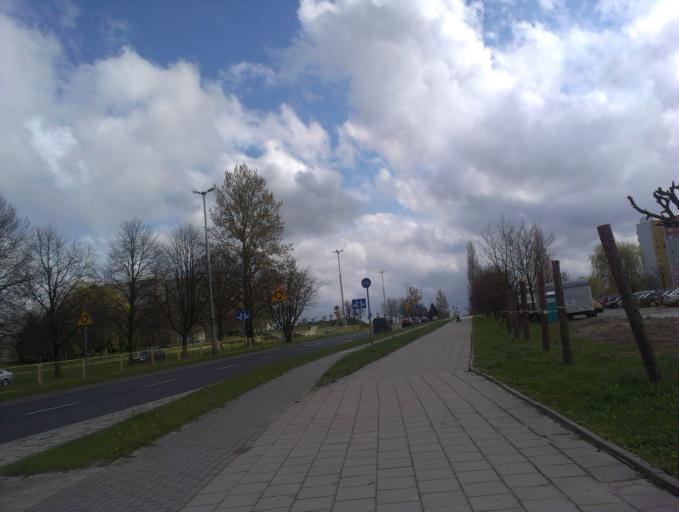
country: PL
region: West Pomeranian Voivodeship
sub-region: Koszalin
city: Koszalin
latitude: 54.2046
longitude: 16.1933
